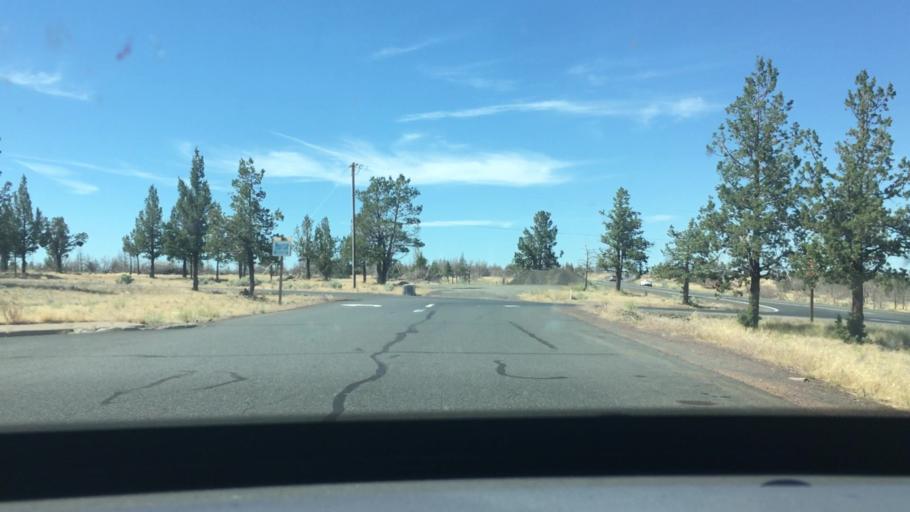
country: US
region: Oregon
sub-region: Jefferson County
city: Madras
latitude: 44.8954
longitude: -120.9360
